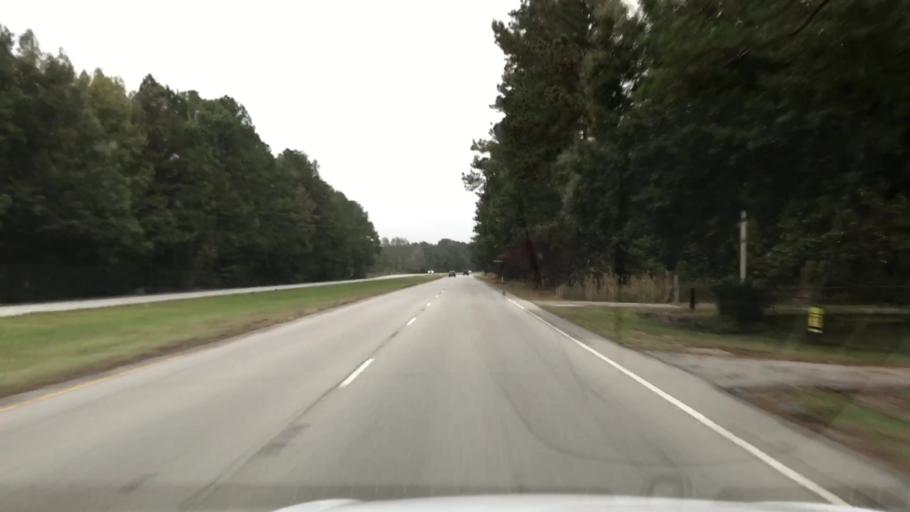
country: US
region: South Carolina
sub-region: Charleston County
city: Awendaw
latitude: 32.9983
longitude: -79.6442
